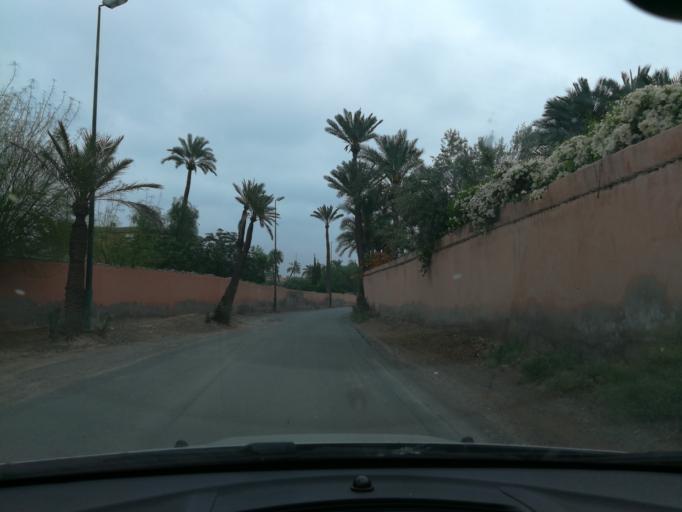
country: MA
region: Marrakech-Tensift-Al Haouz
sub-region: Marrakech
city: Marrakesh
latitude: 31.6844
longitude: -7.9848
